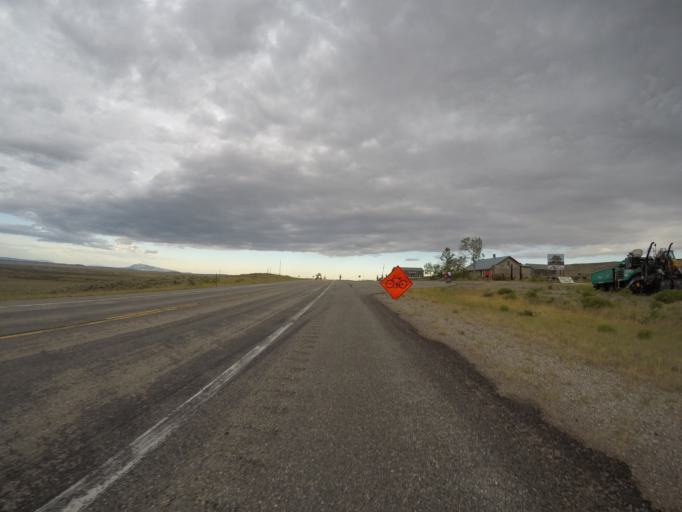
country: US
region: Wyoming
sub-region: Albany County
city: Laramie
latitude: 41.8648
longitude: -106.0723
